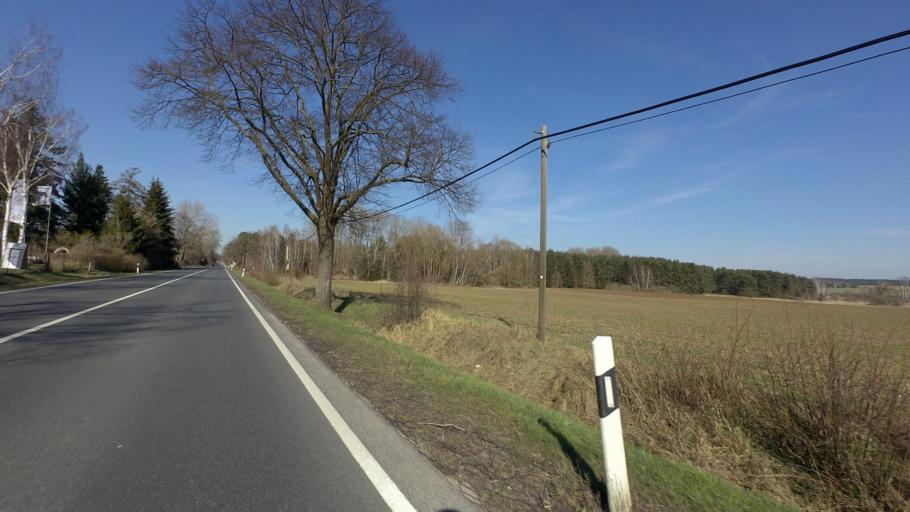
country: DE
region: Brandenburg
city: Angermunde
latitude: 52.9900
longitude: 13.9804
